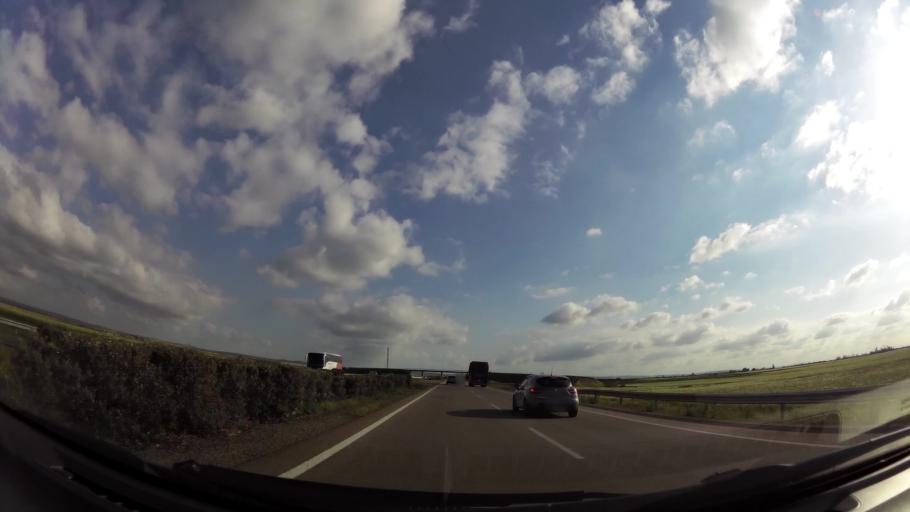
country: MA
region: Chaouia-Ouardigha
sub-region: Settat Province
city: Berrechid
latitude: 33.1499
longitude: -7.5727
